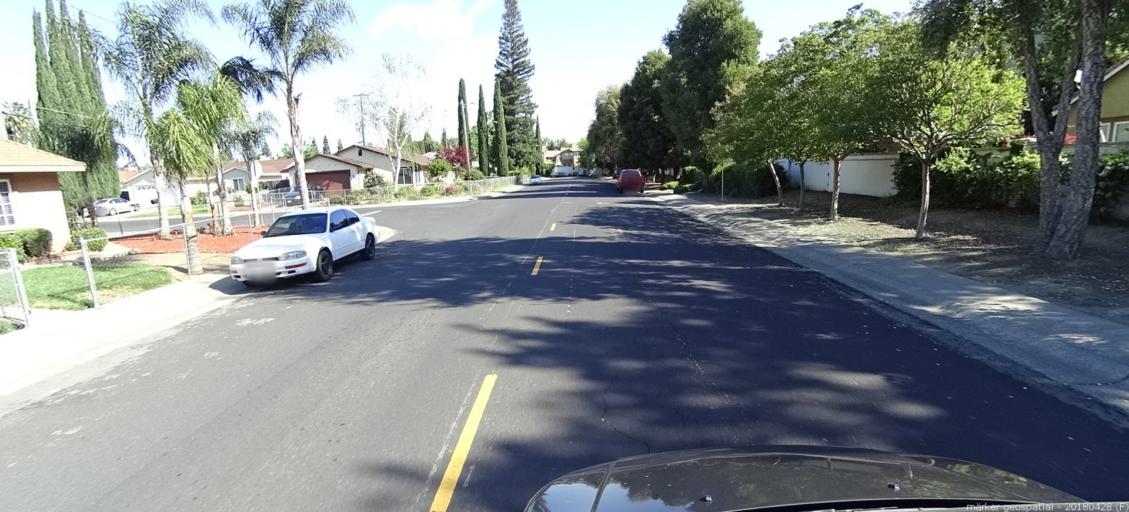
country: US
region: California
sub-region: Yolo County
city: West Sacramento
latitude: 38.5990
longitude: -121.5263
